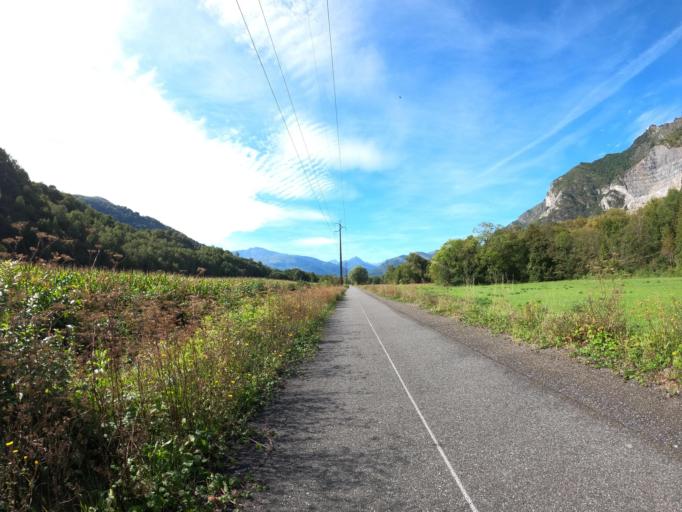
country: FR
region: Midi-Pyrenees
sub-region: Departement des Hautes-Pyrenees
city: Lourdes
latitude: 43.0471
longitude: -0.0521
